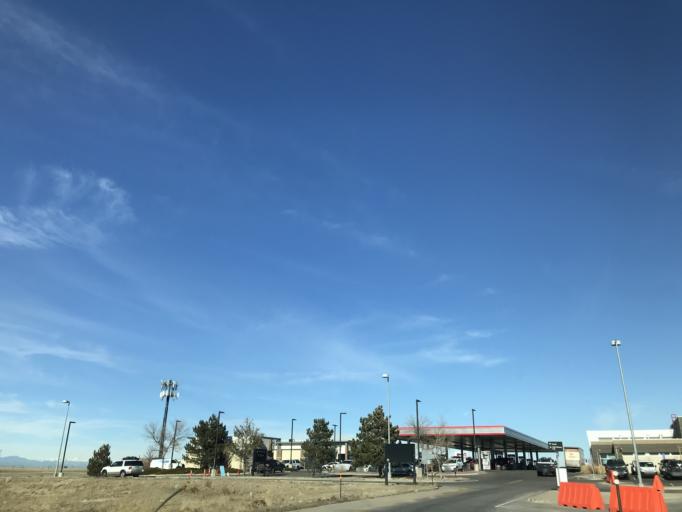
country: US
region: Colorado
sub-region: Adams County
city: Aurora
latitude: 39.8351
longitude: -104.7199
